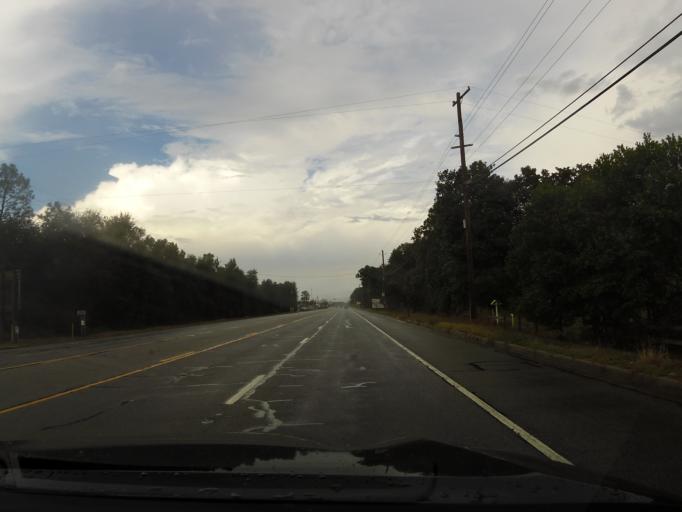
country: US
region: Georgia
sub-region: Wayne County
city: Jesup
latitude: 31.6403
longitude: -81.8594
